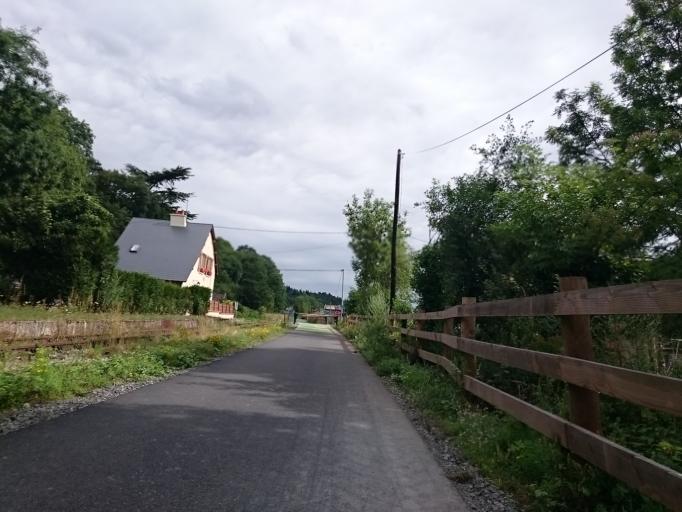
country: FR
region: Lower Normandy
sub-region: Departement du Calvados
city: Thury-Harcourt
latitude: 49.0336
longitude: -0.4659
